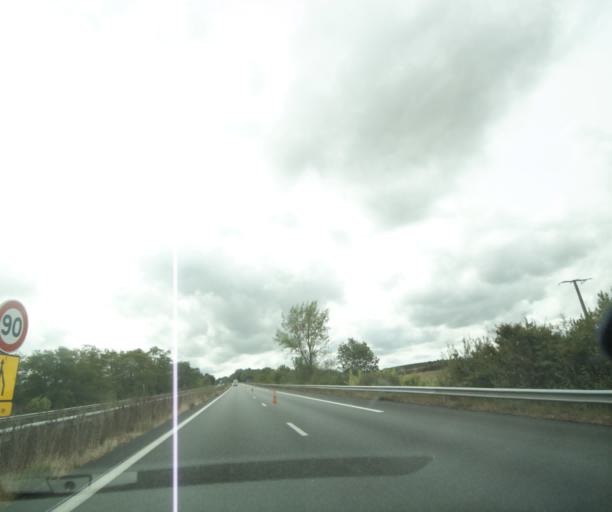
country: FR
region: Poitou-Charentes
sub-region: Departement de la Charente-Maritime
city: Mirambeau
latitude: 45.3609
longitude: -0.5875
